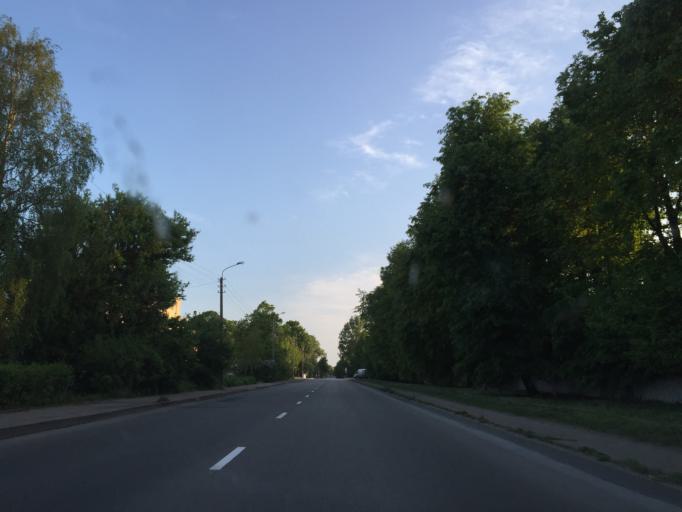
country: LT
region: Siauliu apskritis
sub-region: Siauliai
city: Siauliai
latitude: 55.9522
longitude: 23.3267
